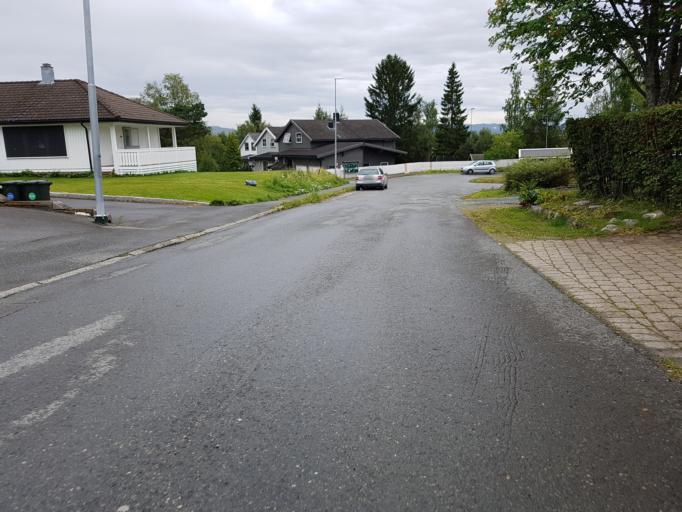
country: NO
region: Sor-Trondelag
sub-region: Trondheim
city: Trondheim
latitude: 63.3889
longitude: 10.3331
